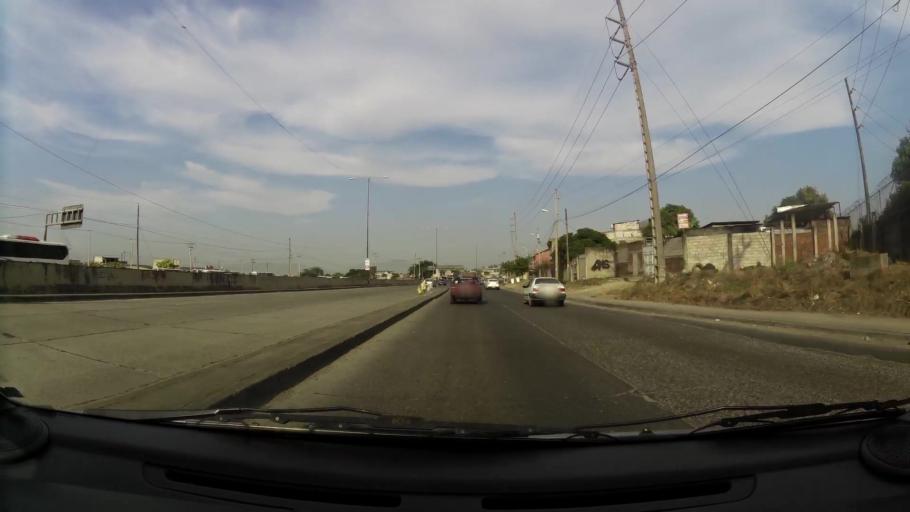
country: EC
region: Guayas
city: Eloy Alfaro
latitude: -2.0771
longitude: -79.9227
